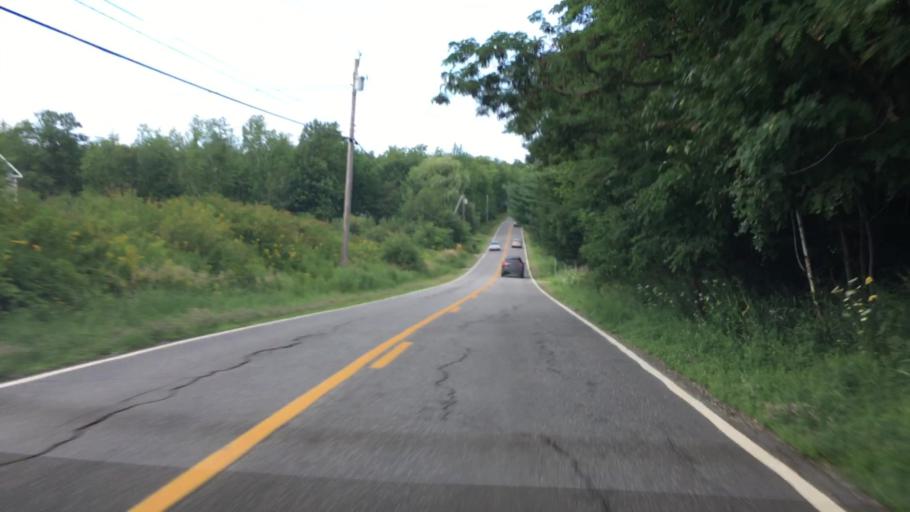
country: US
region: Maine
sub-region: Waldo County
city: Belfast
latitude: 44.3678
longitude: -69.0389
